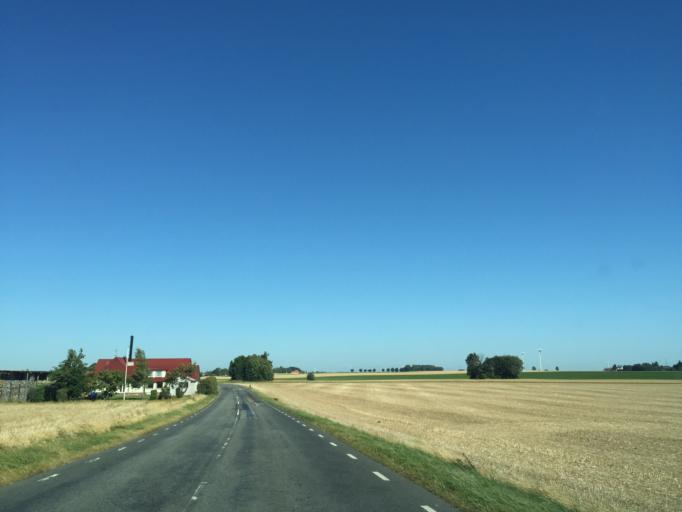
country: SE
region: Skane
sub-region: Ystads Kommun
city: Kopingebro
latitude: 55.4478
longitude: 14.1204
